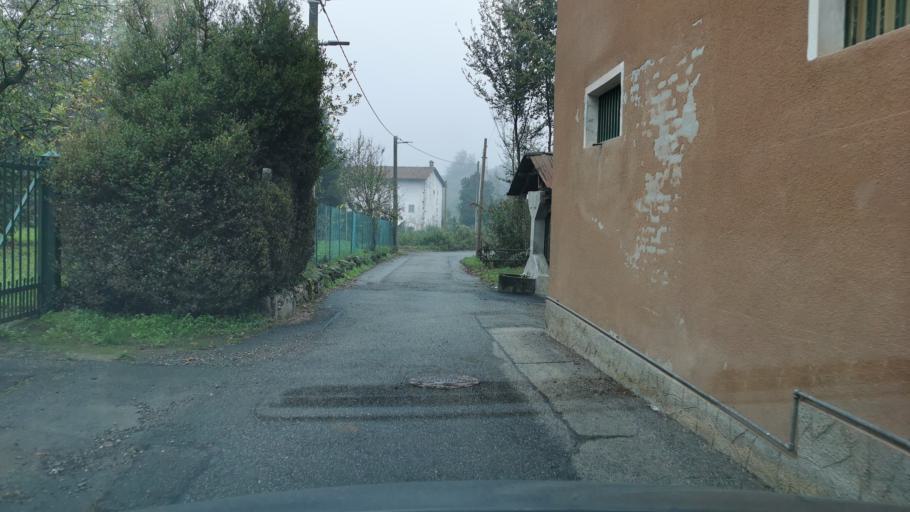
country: IT
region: Piedmont
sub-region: Provincia di Torino
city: Scarmagno
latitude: 45.3795
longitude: 7.8339
